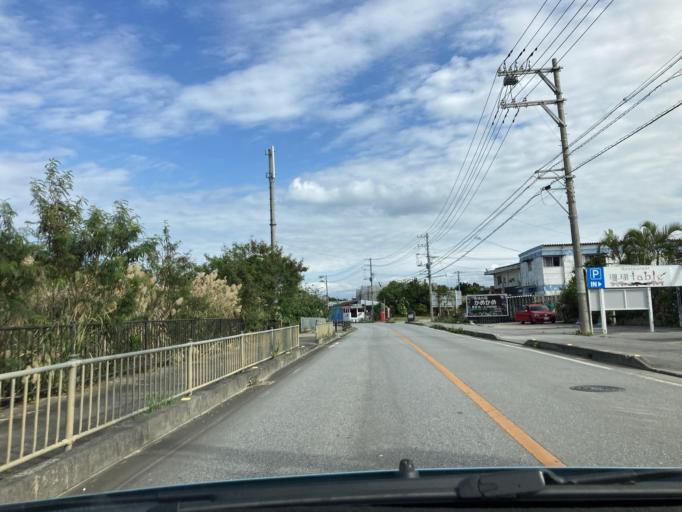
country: JP
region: Okinawa
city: Nago
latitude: 26.6959
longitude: 127.9468
